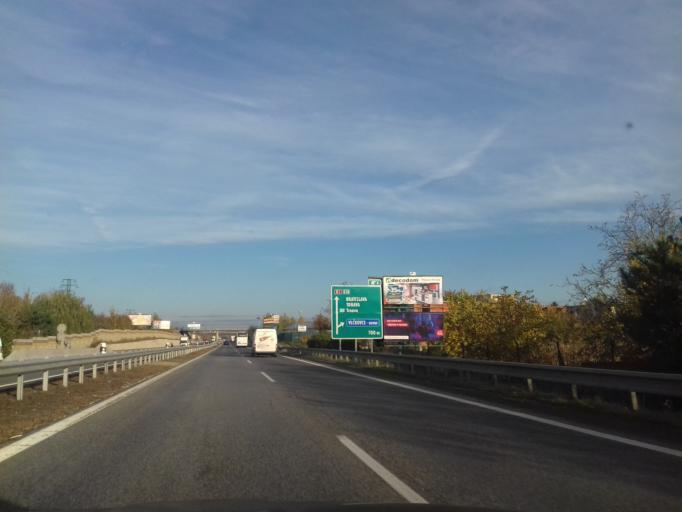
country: SK
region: Trnavsky
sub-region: Okres Trnava
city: Trnava
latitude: 48.3071
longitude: 17.6515
